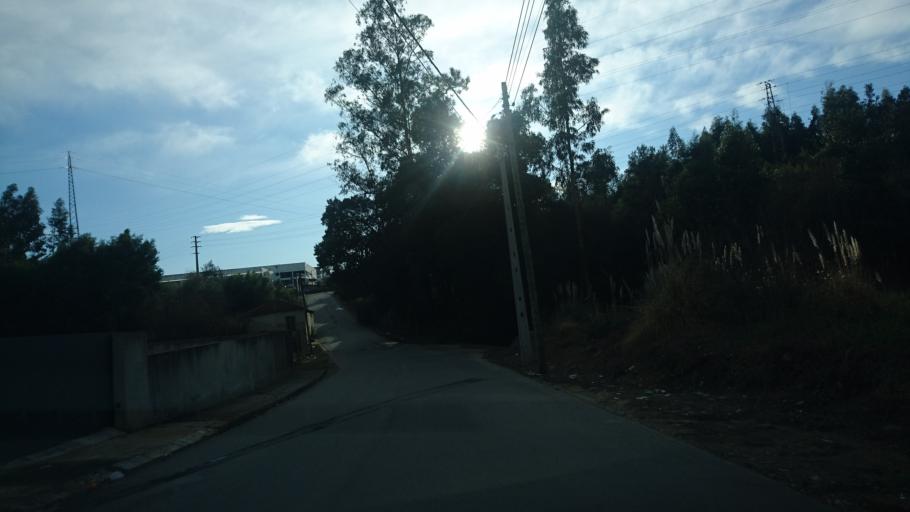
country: PT
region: Aveiro
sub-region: Santa Maria da Feira
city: Pacos de Brandao
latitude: 40.9664
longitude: -8.5956
